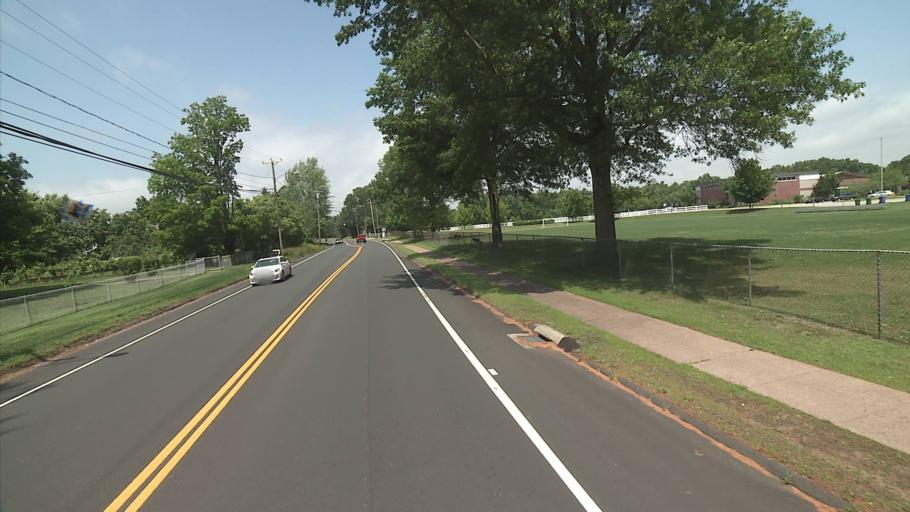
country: US
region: Connecticut
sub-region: Hartford County
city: Glastonbury Center
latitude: 41.7173
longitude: -72.5586
